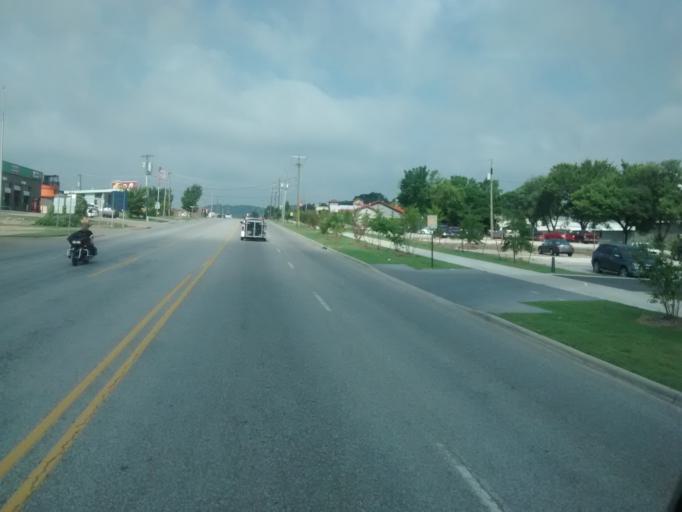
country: US
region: Arkansas
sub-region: Washington County
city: Fayetteville
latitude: 36.0567
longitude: -94.1809
